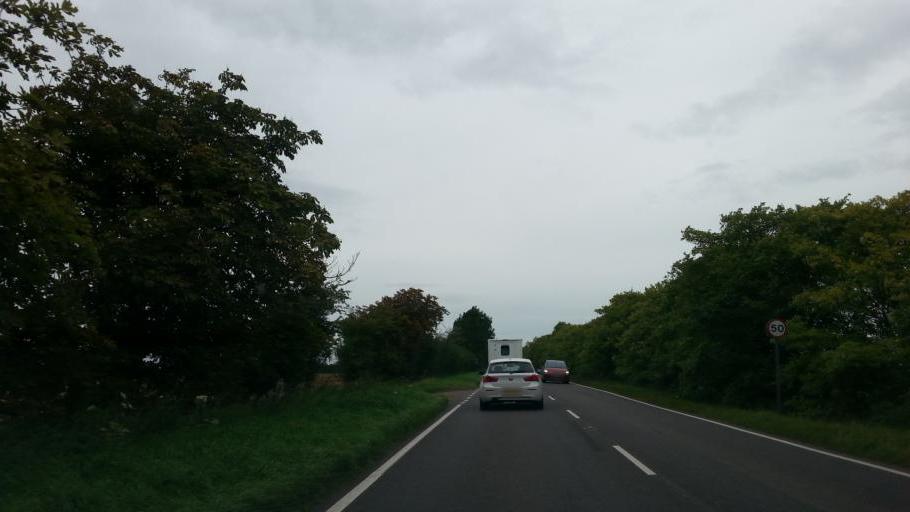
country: GB
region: England
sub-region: Cambridgeshire
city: Papworth Everard
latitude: 52.2220
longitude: -0.0998
